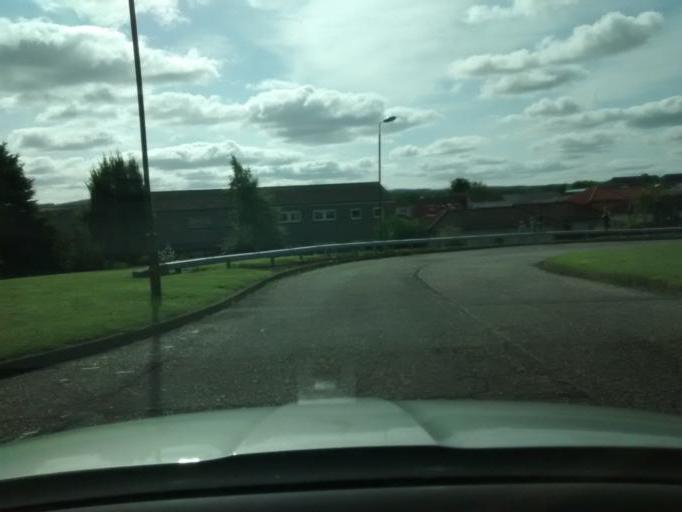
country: GB
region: Scotland
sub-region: West Lothian
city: Mid Calder
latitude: 55.8963
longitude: -3.4964
